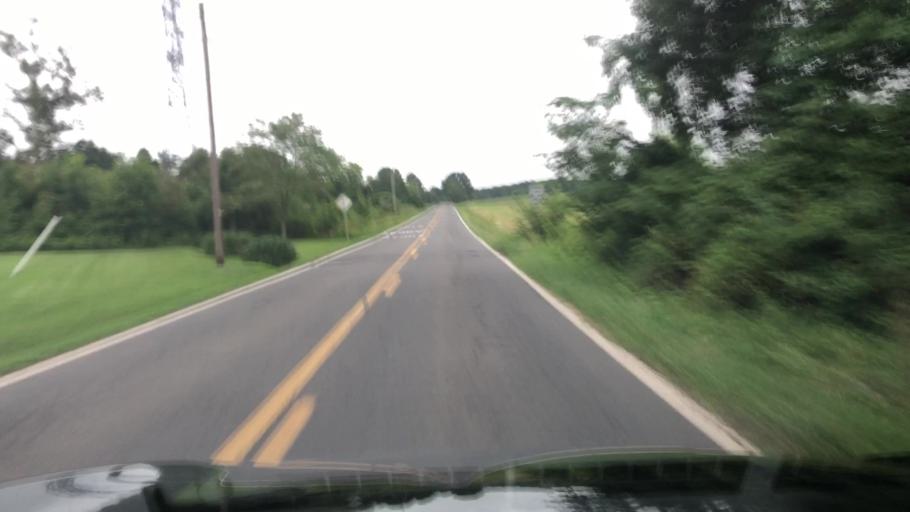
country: US
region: Virginia
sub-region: Prince William County
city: Nokesville
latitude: 38.5829
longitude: -77.6137
